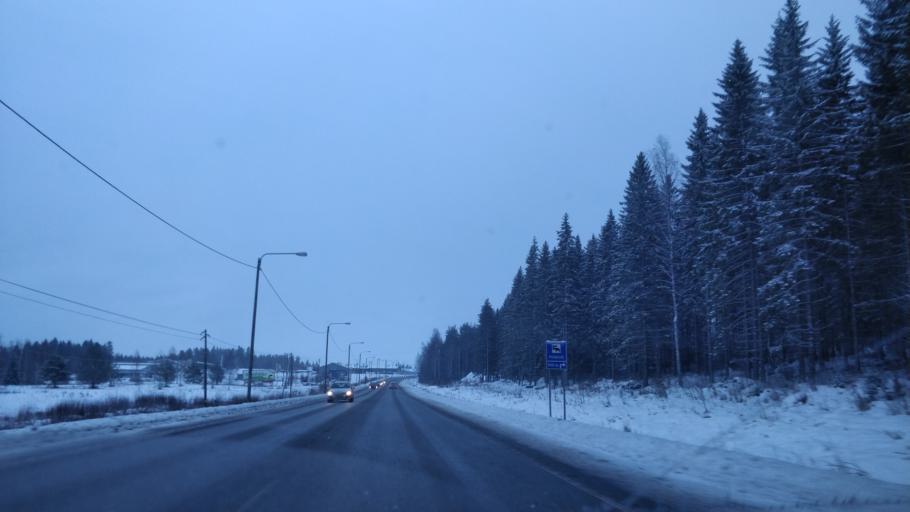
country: FI
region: Central Finland
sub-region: Saarijaervi-Viitasaari
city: Viitasaari
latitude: 63.0927
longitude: 25.8549
